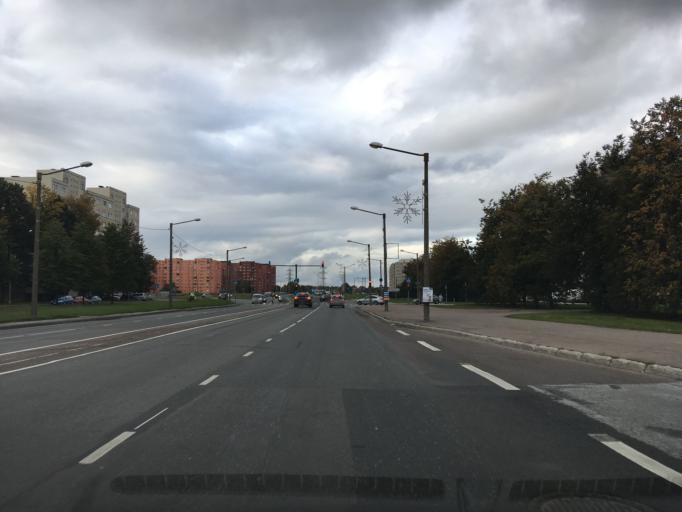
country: EE
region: Harju
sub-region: Tallinna linn
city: Kose
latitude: 59.4369
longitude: 24.8284
